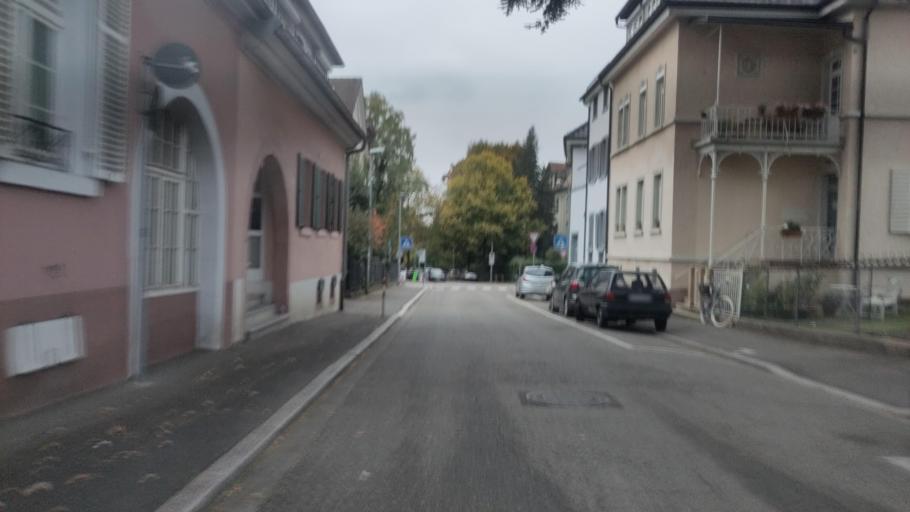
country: DE
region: Baden-Wuerttemberg
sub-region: Freiburg Region
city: Freiburg
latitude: 48.0043
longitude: 7.8637
